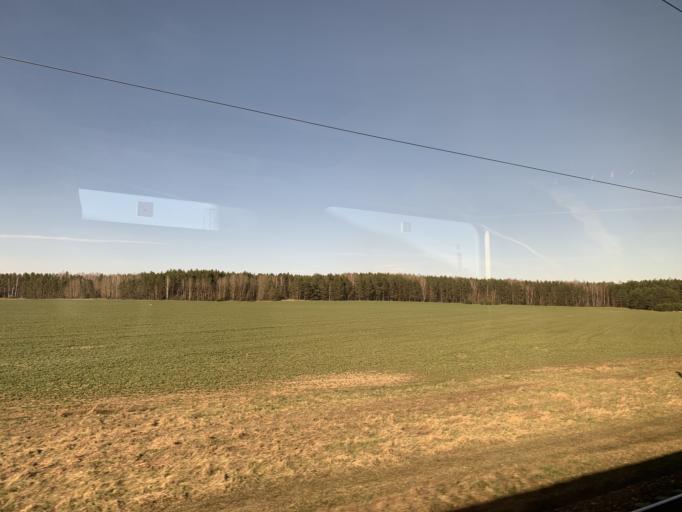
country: BY
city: Soly
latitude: 54.4944
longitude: 26.2777
